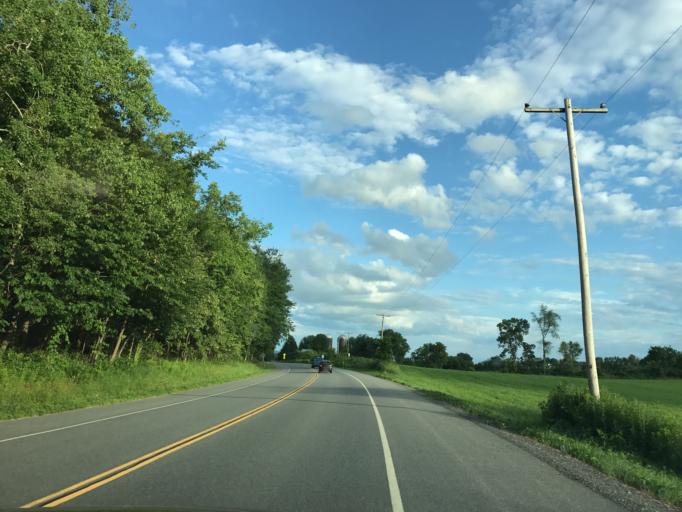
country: US
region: New York
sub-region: Saratoga County
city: Schuylerville
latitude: 43.0549
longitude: -73.5951
